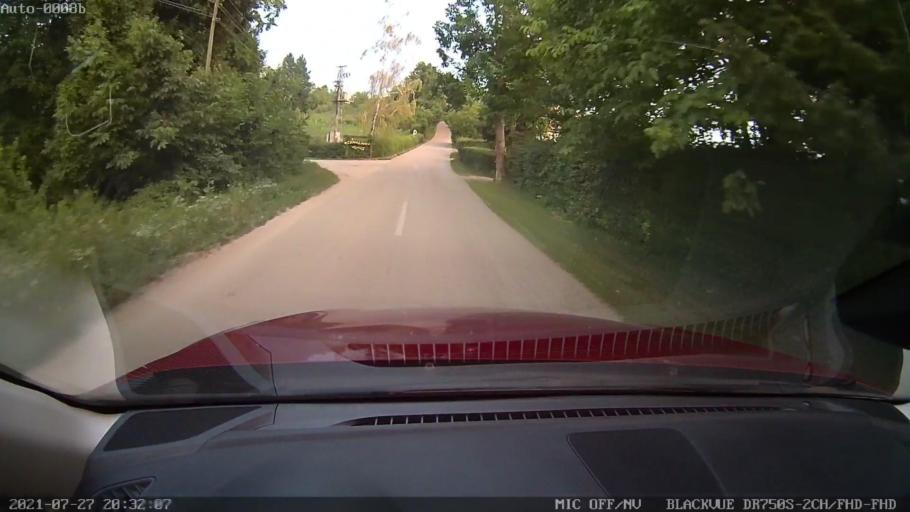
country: HR
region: Varazdinska
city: Jalzabet
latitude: 46.2448
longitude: 16.4750
